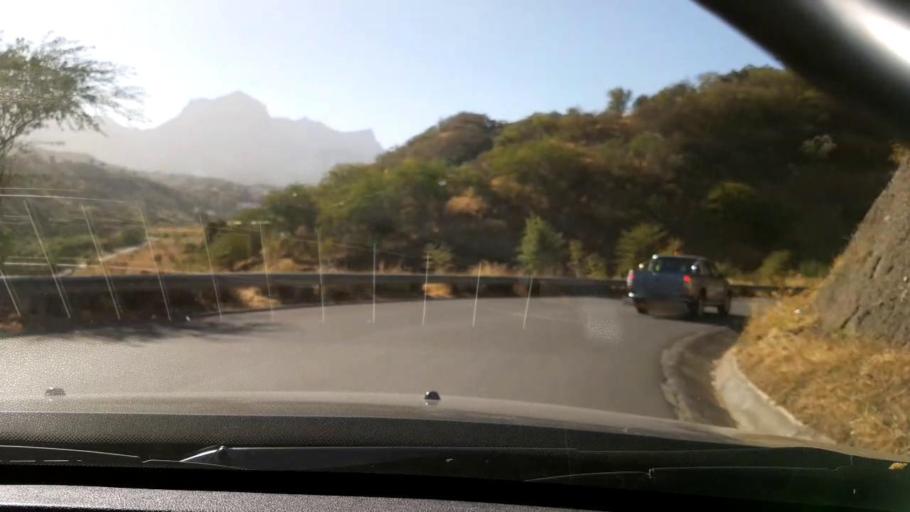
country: CV
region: Sao Lourenco dos Orgaos
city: Joao Teves
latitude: 15.0715
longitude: -23.5686
